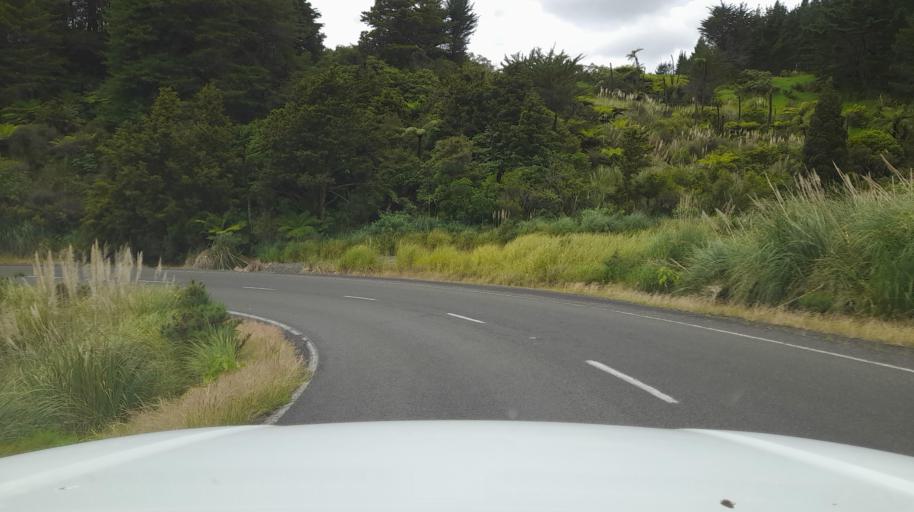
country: NZ
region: Northland
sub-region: Far North District
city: Kaitaia
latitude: -35.3667
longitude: 173.4341
